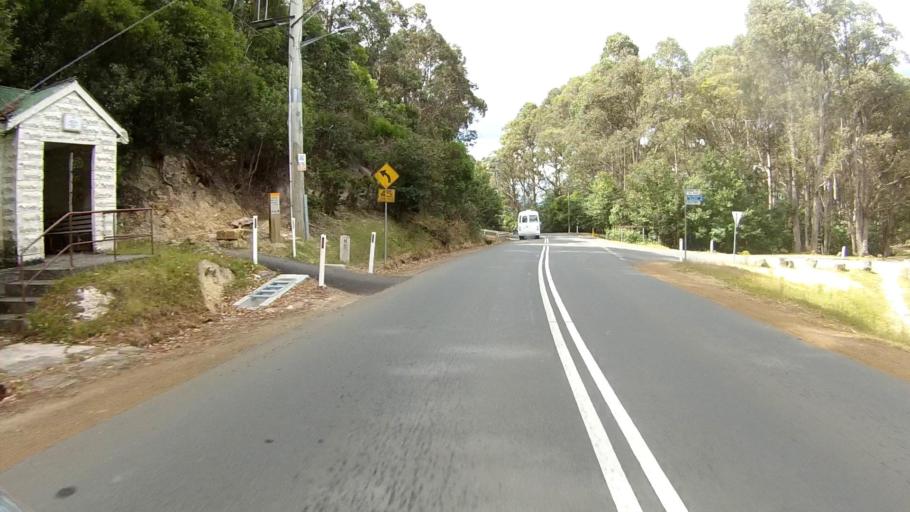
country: AU
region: Tasmania
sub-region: Hobart
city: Dynnyrne
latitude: -42.9190
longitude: 147.2682
